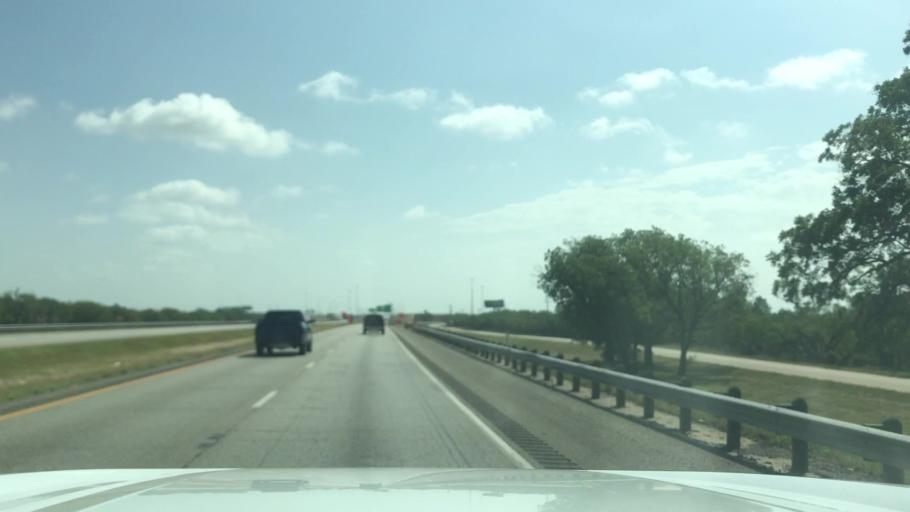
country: US
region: Texas
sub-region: Taylor County
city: Abilene
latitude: 32.4790
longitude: -99.7826
